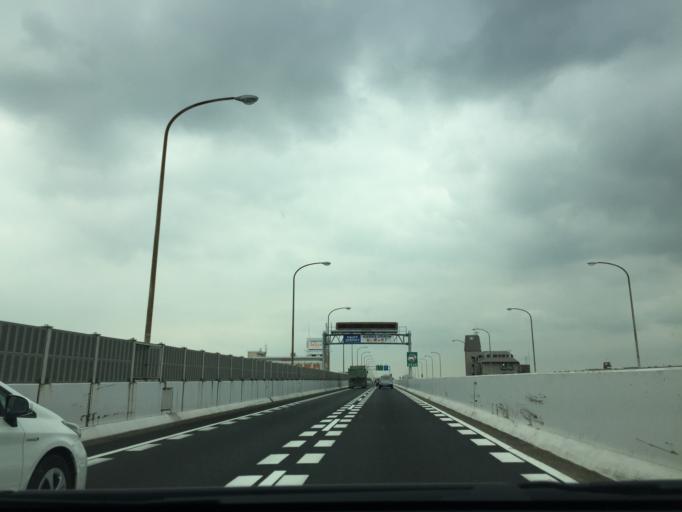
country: JP
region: Aichi
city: Nagoya-shi
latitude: 35.1058
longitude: 136.9234
